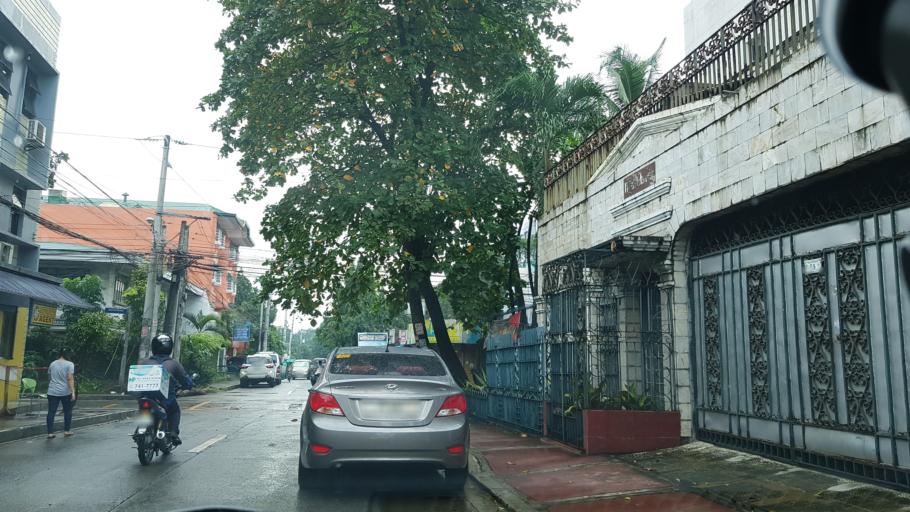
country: PH
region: Metro Manila
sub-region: Quezon City
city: Quezon City
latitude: 14.6406
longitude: 121.0494
